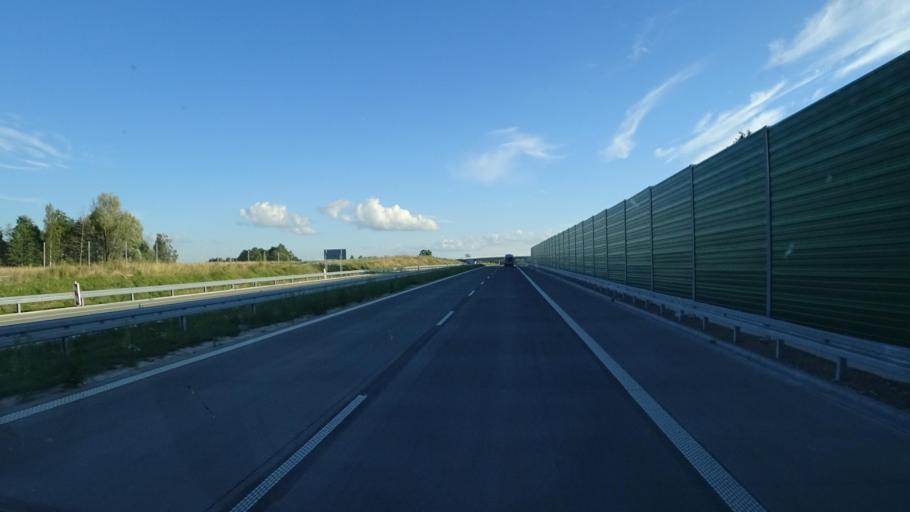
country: PL
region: Podlasie
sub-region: Powiat suwalski
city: Raczki
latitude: 53.9464
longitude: 22.7653
